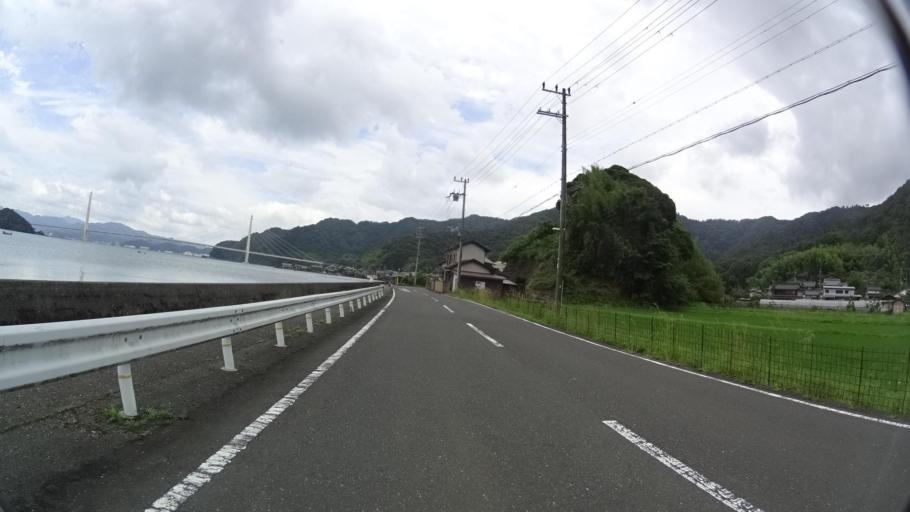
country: JP
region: Kyoto
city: Maizuru
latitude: 35.5073
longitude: 135.3775
